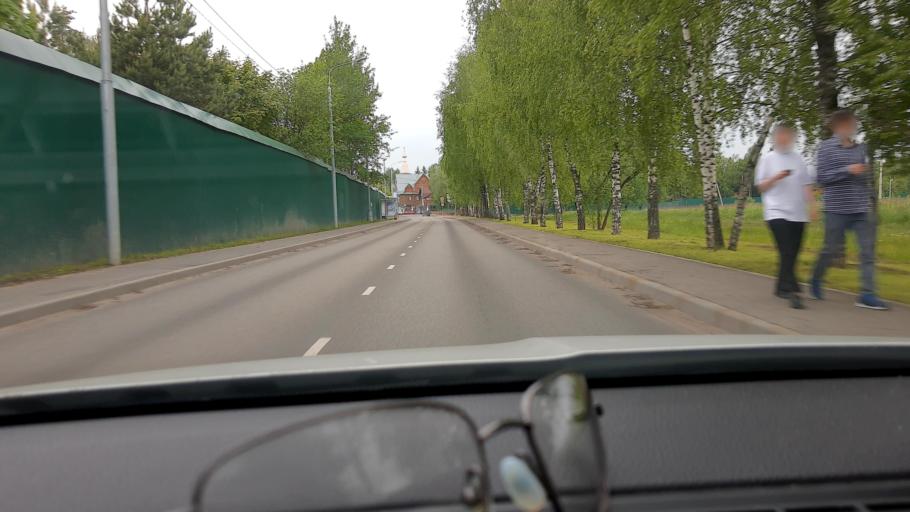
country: RU
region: Moskovskaya
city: Vatutinki
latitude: 55.5151
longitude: 37.3389
